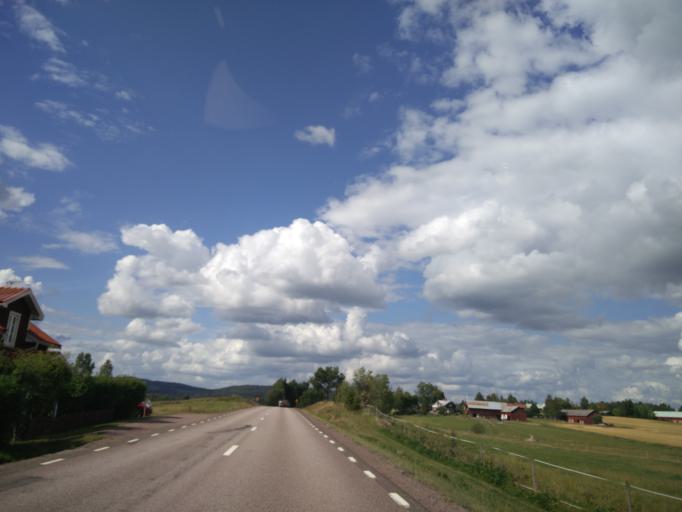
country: SE
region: Vaermland
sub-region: Sunne Kommun
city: Sunne
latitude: 59.7125
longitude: 13.1044
